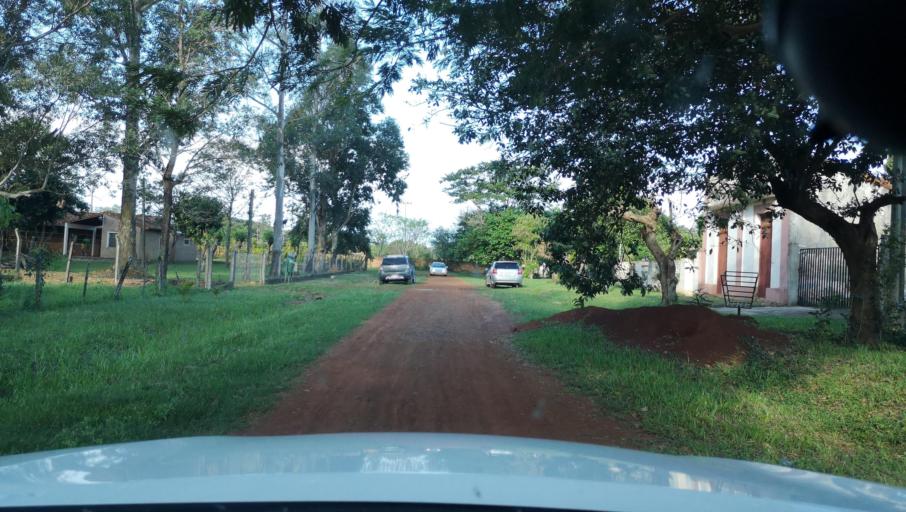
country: PY
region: Itapua
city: Carmen del Parana
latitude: -27.1605
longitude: -56.2445
